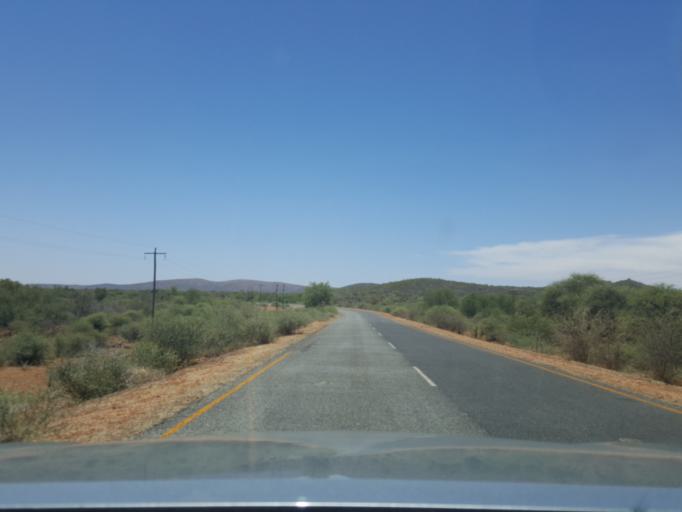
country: BW
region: South East
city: Ramotswa
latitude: -24.8867
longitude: 25.8894
